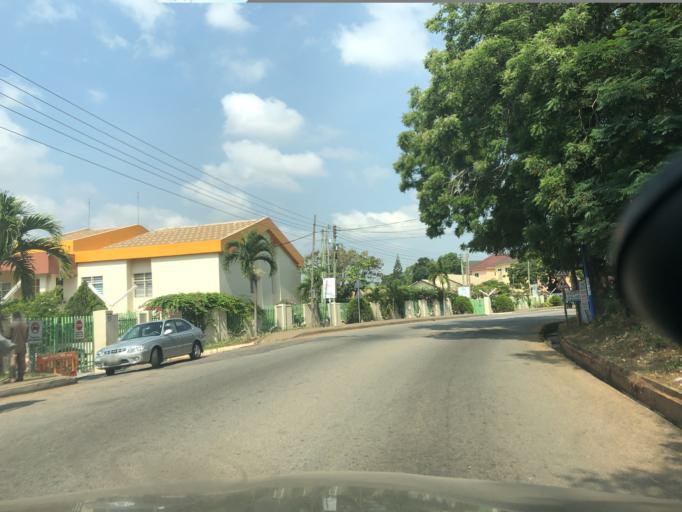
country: GH
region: Greater Accra
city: Accra
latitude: 5.5806
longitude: -0.1758
